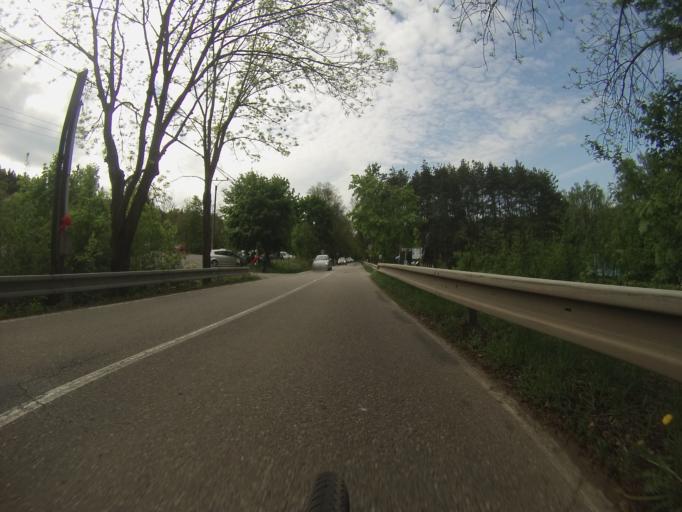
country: CZ
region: South Moravian
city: Kurim
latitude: 49.2425
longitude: 16.4991
